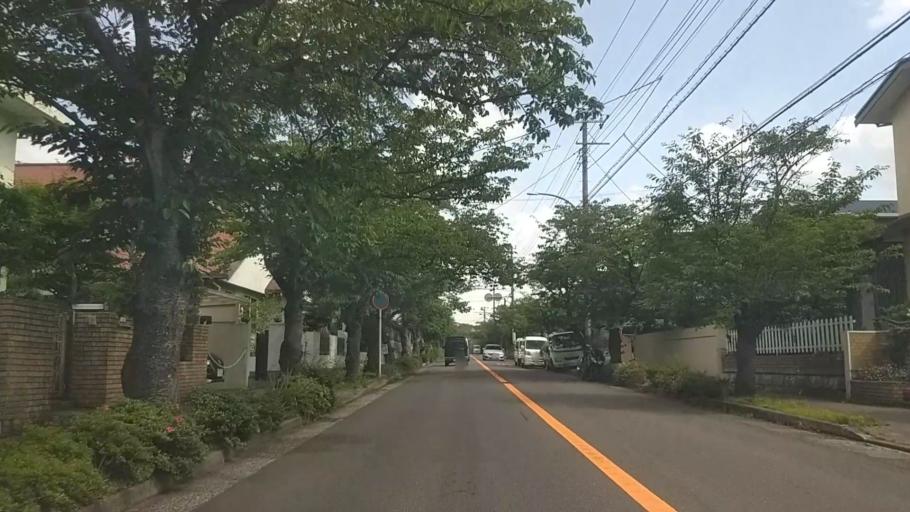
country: JP
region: Kanagawa
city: Zushi
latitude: 35.3125
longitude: 139.5769
